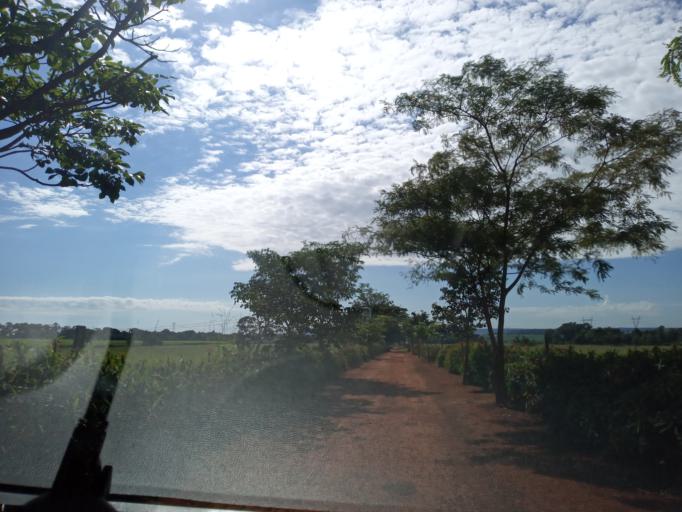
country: BR
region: Goias
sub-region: Itumbiara
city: Itumbiara
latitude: -18.4600
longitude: -49.1186
